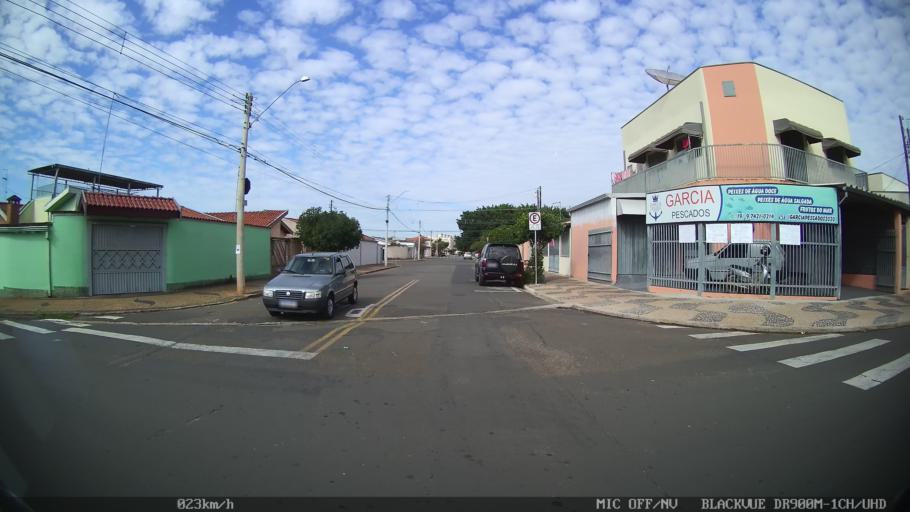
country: BR
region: Sao Paulo
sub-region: Santa Barbara D'Oeste
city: Santa Barbara d'Oeste
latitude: -22.7681
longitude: -47.3920
